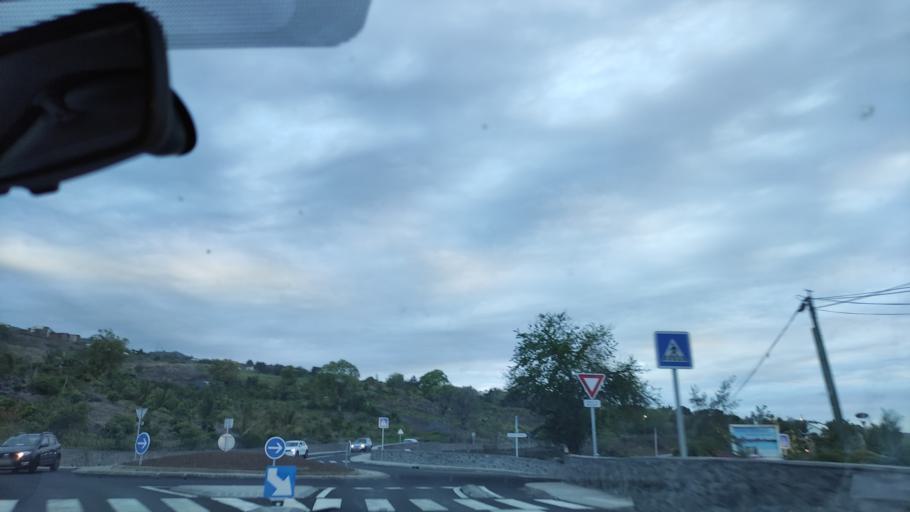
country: RE
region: Reunion
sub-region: Reunion
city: Saint-Leu
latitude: -21.1922
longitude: 55.2903
